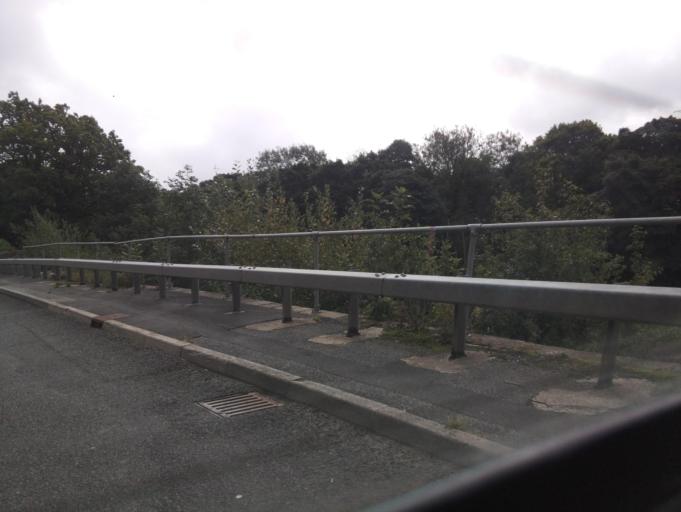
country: GB
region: England
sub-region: Kirklees
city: Holmfirth
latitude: 53.5734
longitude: -1.7463
